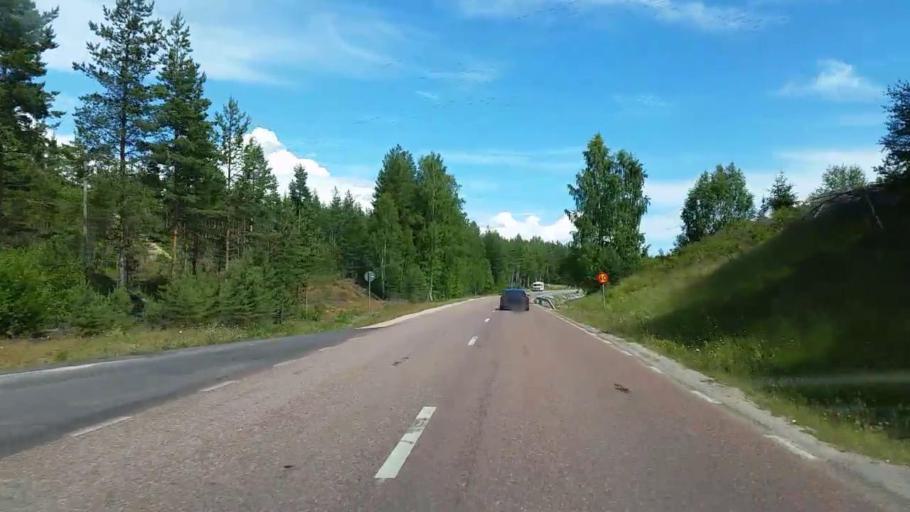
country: SE
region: Dalarna
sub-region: Rattviks Kommun
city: Raettvik
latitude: 61.1713
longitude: 15.1511
